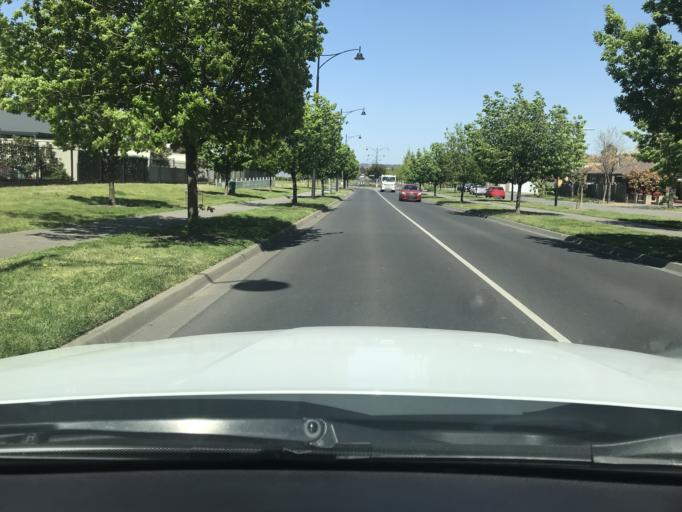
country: AU
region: Victoria
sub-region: Hume
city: Roxburgh Park
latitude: -37.5877
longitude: 144.9061
